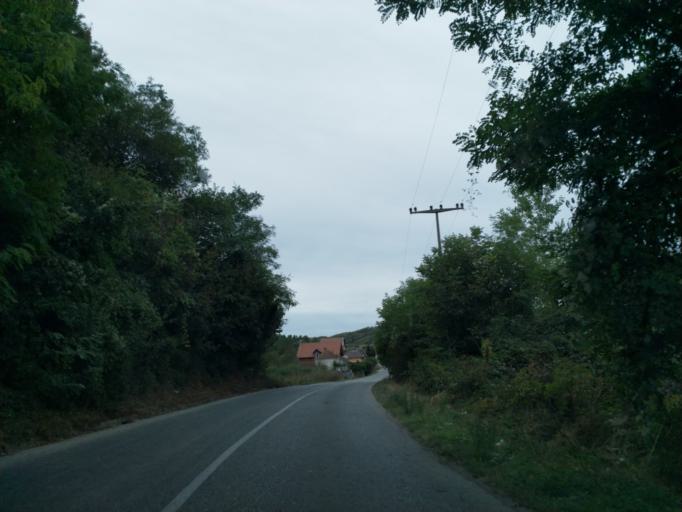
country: RS
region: Central Serbia
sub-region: Pomoravski Okrug
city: Jagodina
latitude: 44.0597
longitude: 21.1822
